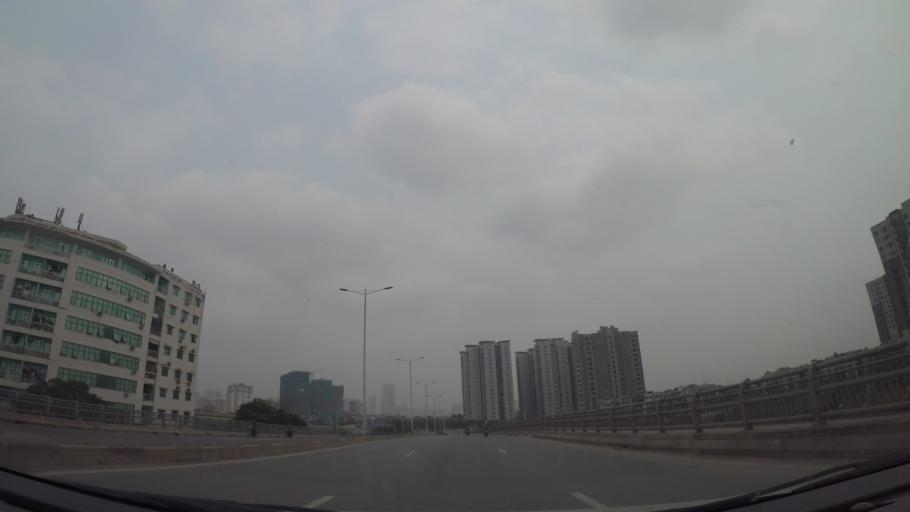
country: VN
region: Ha Noi
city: Cau Dien
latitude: 21.0339
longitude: 105.7528
